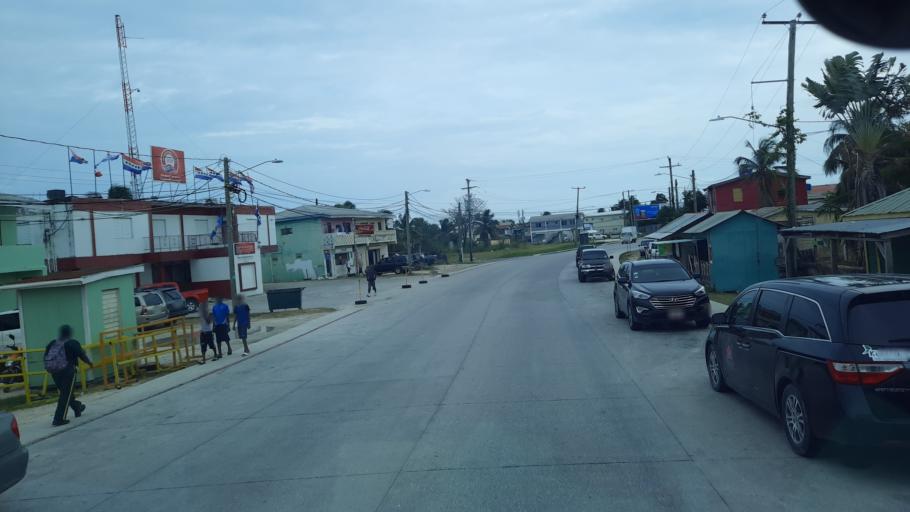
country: BZ
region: Belize
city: Belize City
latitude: 17.4985
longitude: -88.1928
